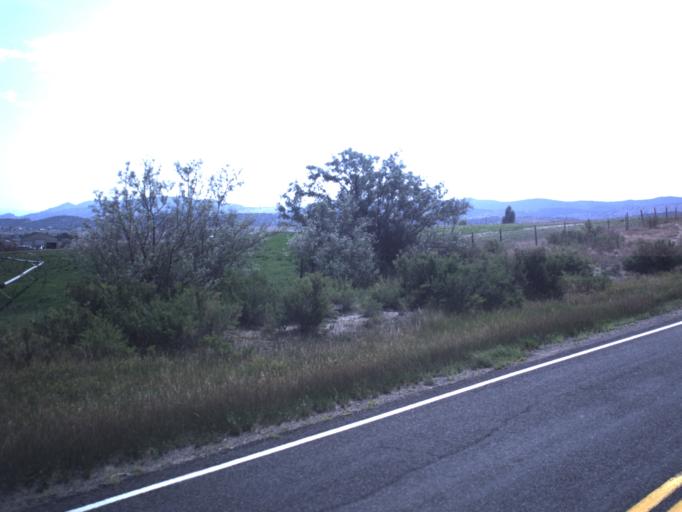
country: US
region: Utah
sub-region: Daggett County
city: Manila
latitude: 40.9752
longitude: -109.7217
